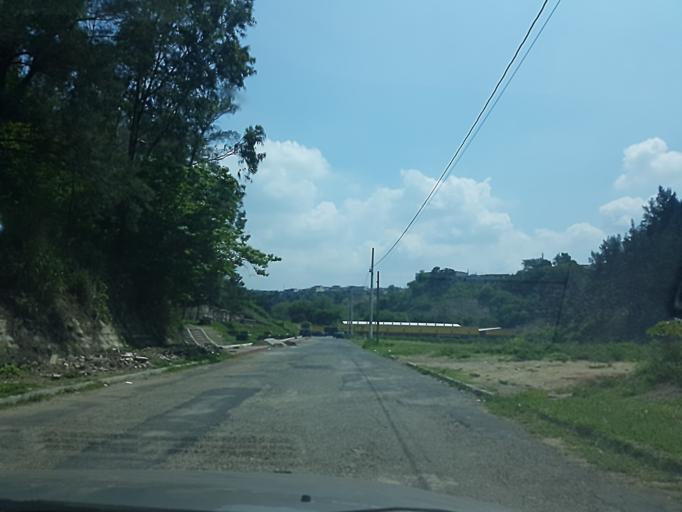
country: GT
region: Guatemala
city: Petapa
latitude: 14.5268
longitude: -90.5496
